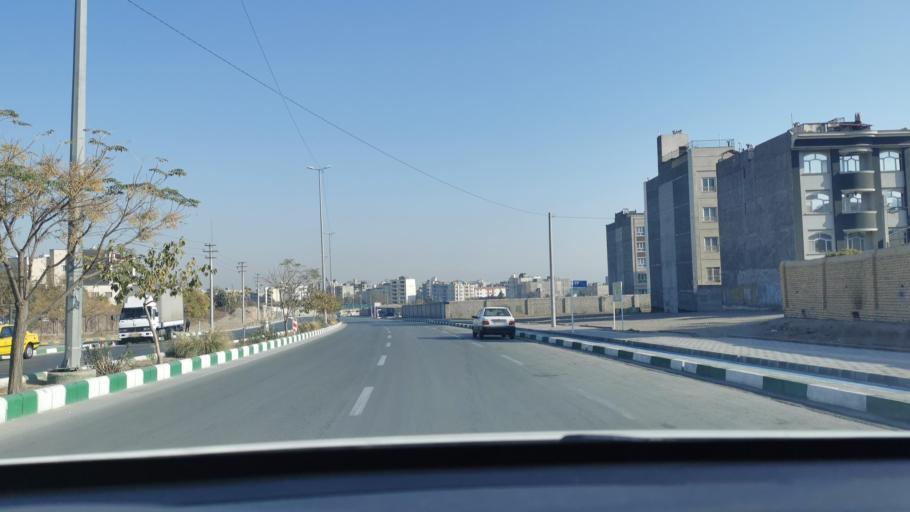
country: IR
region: Razavi Khorasan
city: Mashhad
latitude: 36.2784
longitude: 59.5410
